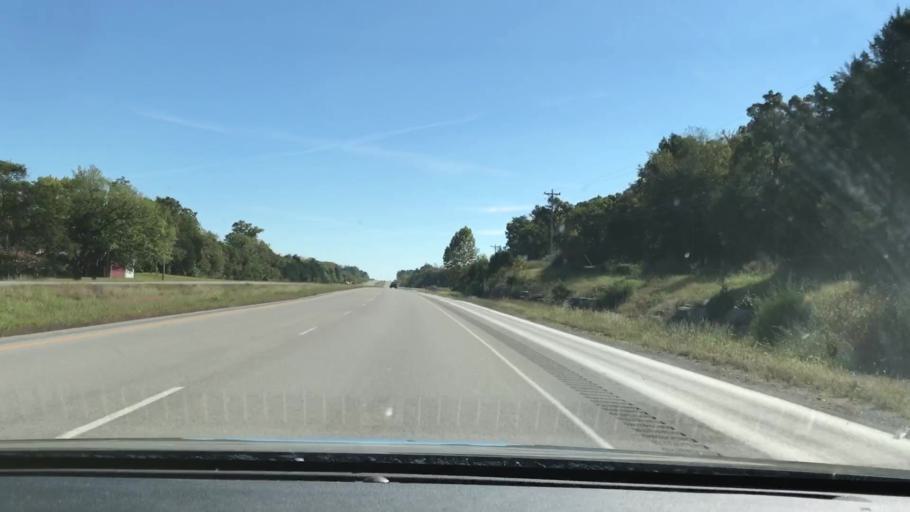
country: US
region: Kentucky
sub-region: Christian County
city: Hopkinsville
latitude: 36.8478
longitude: -87.3307
